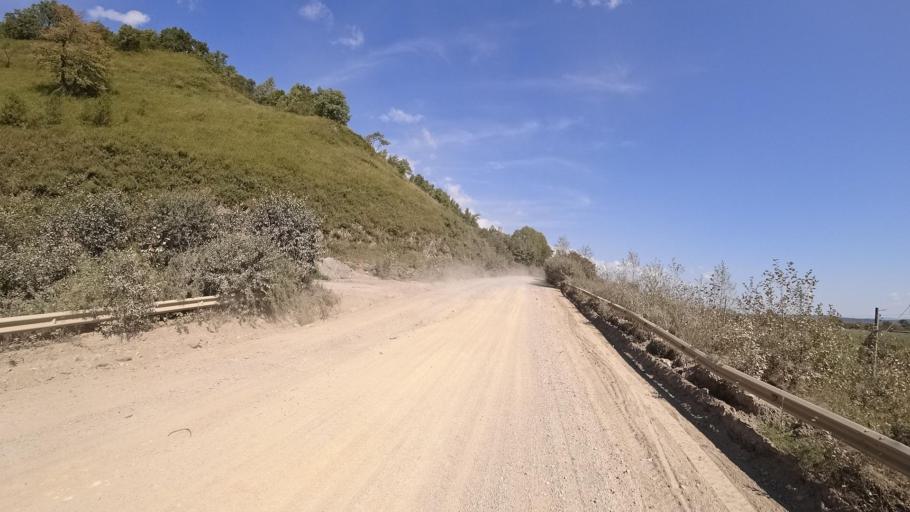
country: RU
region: Jewish Autonomous Oblast
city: Londoko
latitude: 49.0029
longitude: 131.9280
